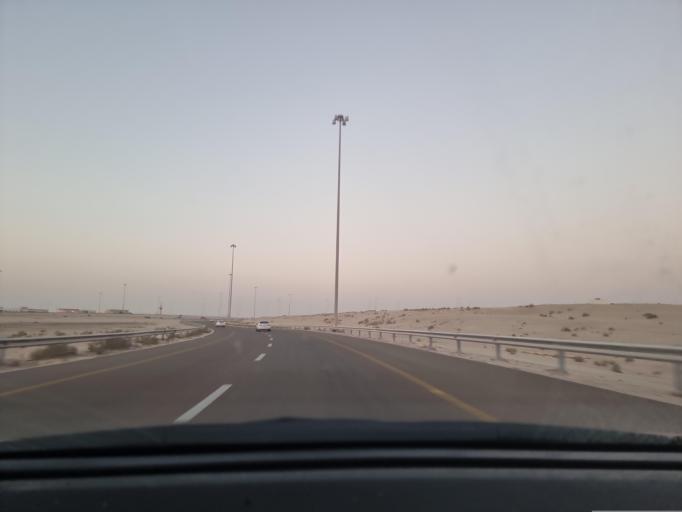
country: AE
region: Abu Dhabi
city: Abu Dhabi
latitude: 24.3766
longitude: 54.7353
